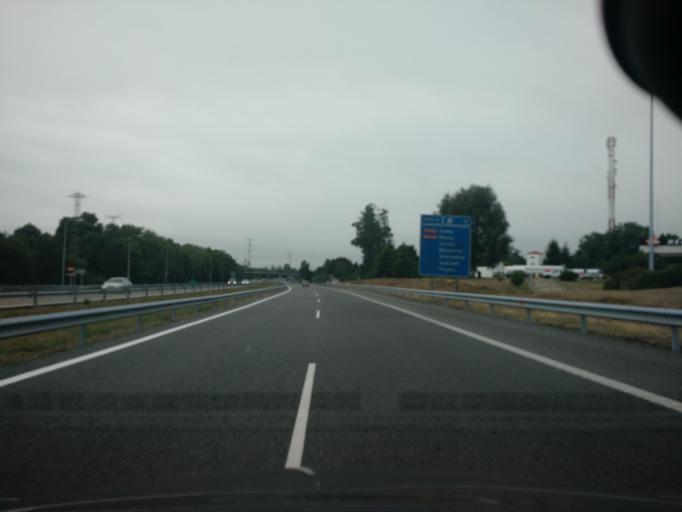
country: ES
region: Galicia
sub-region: Provincia da Coruna
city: Ordes
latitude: 43.0983
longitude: -8.3506
